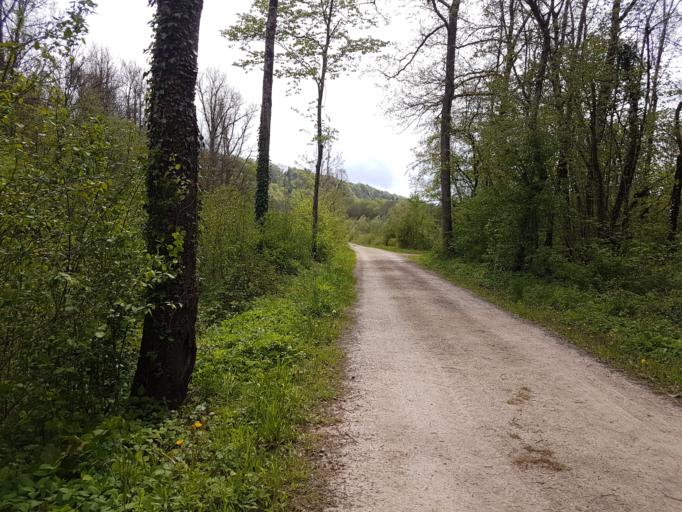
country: CH
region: Schaffhausen
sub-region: Bezirk Schleitheim
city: Schleitheim
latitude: 47.7580
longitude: 8.4681
